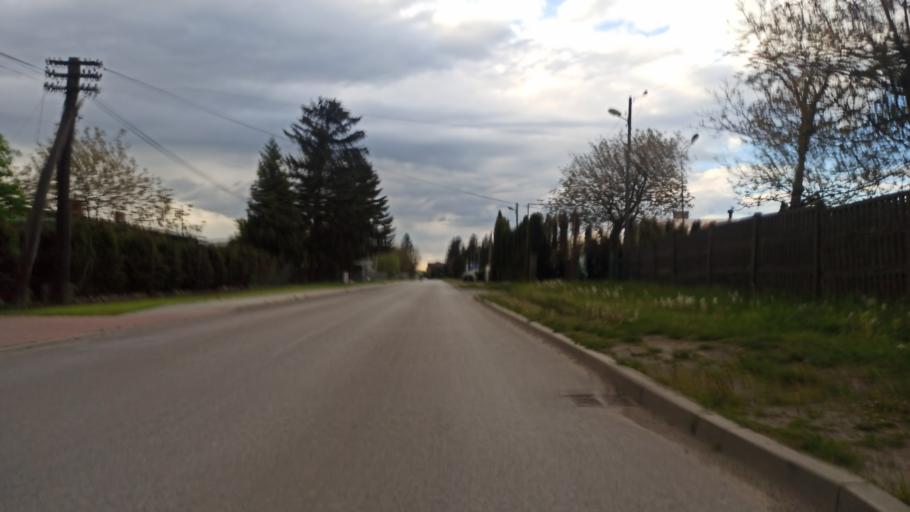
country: PL
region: Subcarpathian Voivodeship
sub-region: Powiat jaroslawski
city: Radymno
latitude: 49.9378
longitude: 22.8352
